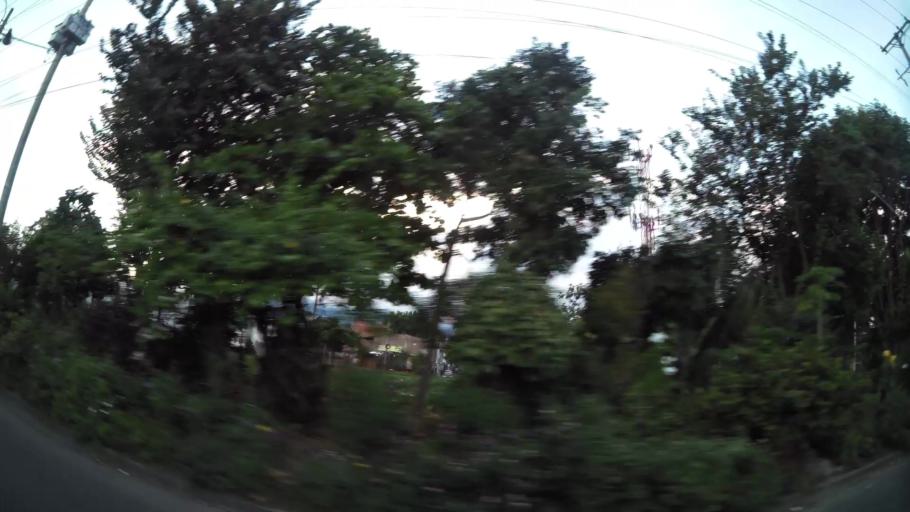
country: CO
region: Valle del Cauca
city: Cali
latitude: 3.4329
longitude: -76.4837
